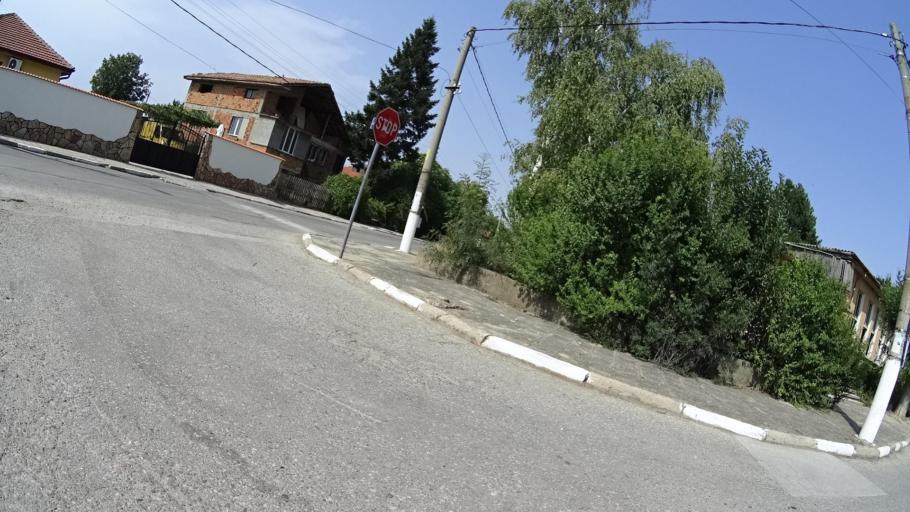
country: BG
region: Plovdiv
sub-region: Obshtina Plovdiv
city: Plovdiv
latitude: 42.2179
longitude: 24.7836
